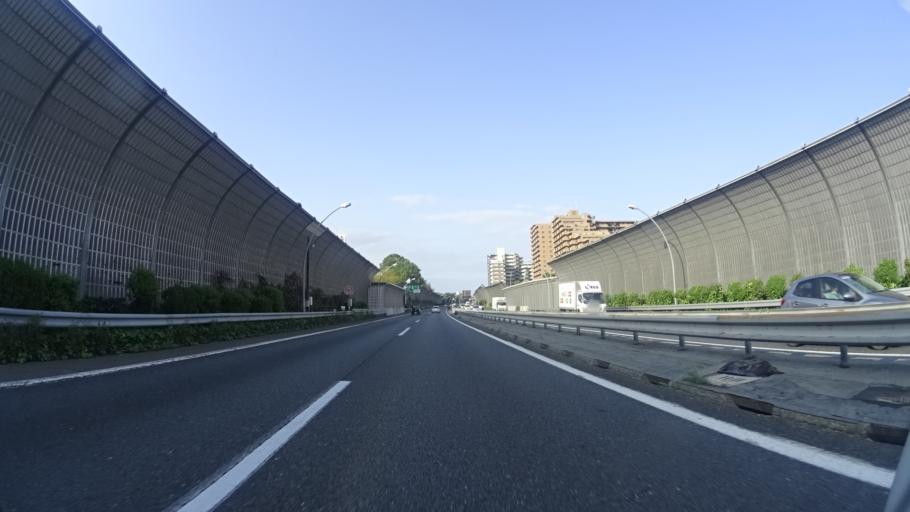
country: JP
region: Osaka
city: Suita
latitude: 34.7921
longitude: 135.5358
